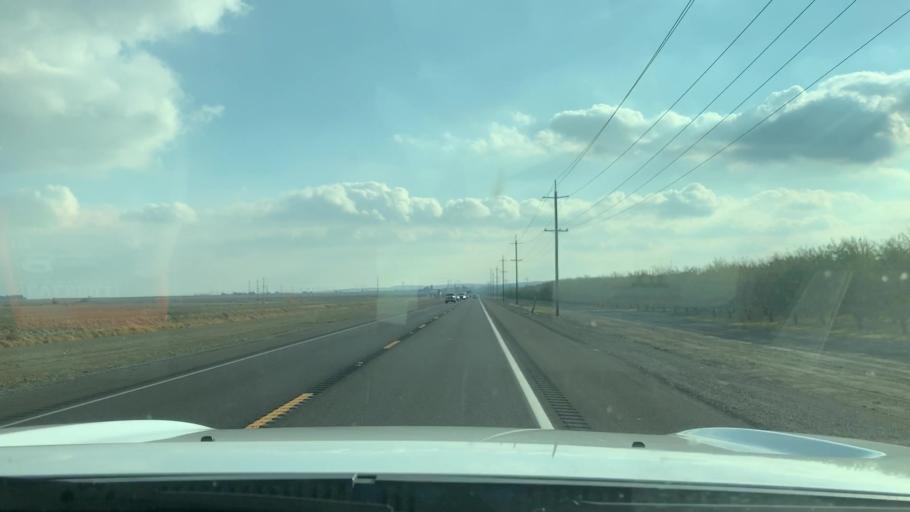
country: US
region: California
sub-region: Kings County
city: Kettleman City
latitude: 36.0278
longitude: -119.9591
